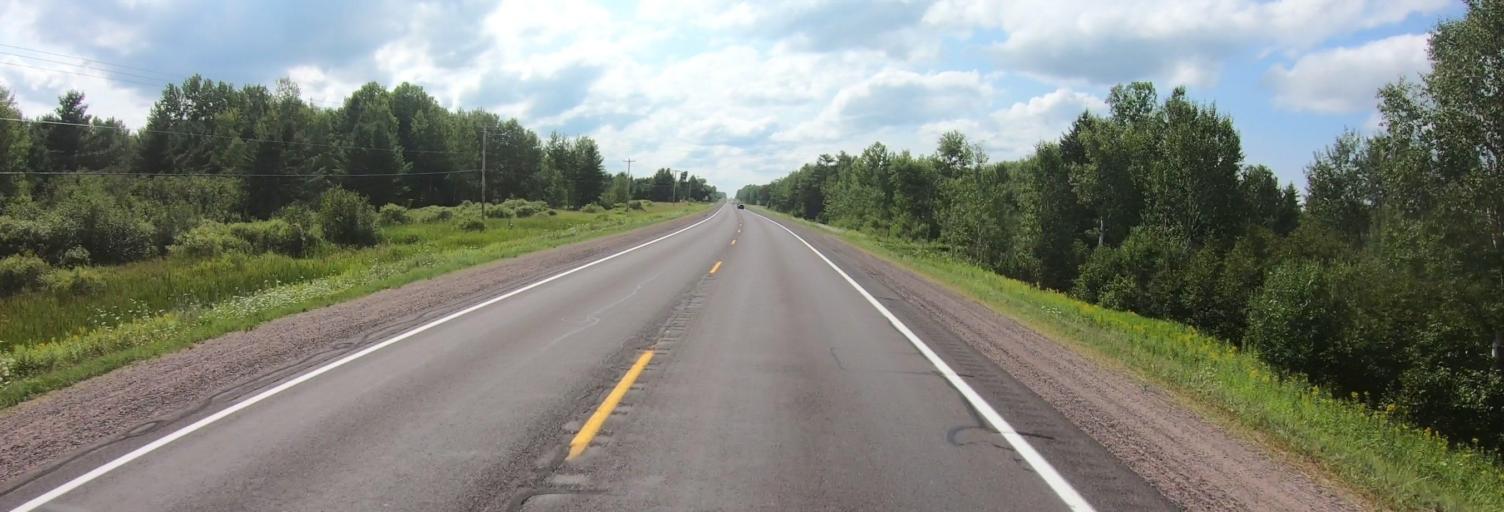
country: US
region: Michigan
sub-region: Ontonagon County
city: Ontonagon
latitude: 46.5348
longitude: -89.2144
